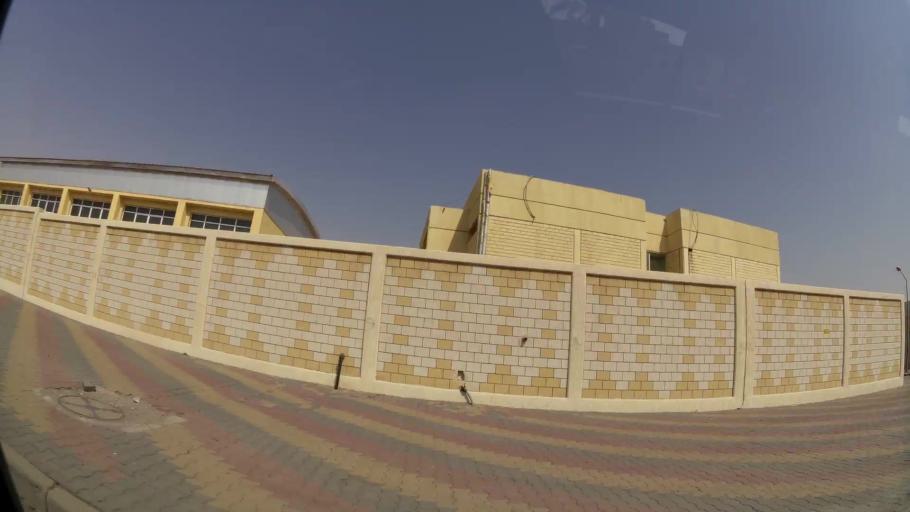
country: KW
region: Muhafazat al Jahra'
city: Al Jahra'
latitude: 29.3376
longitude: 47.6944
